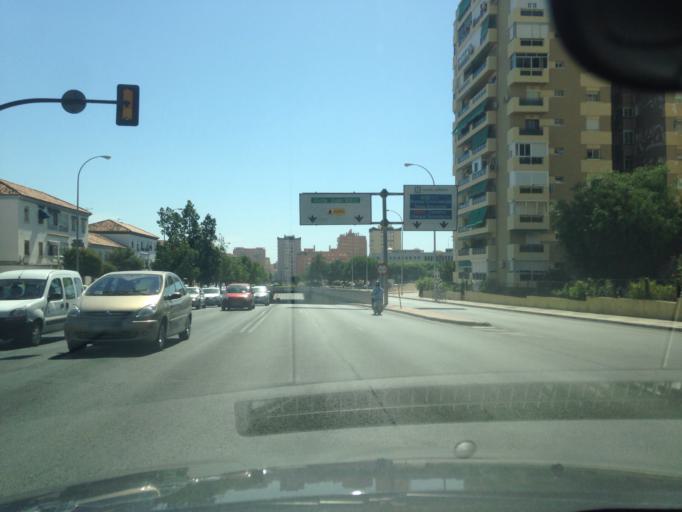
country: ES
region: Andalusia
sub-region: Provincia de Malaga
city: Malaga
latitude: 36.7173
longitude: -4.4487
